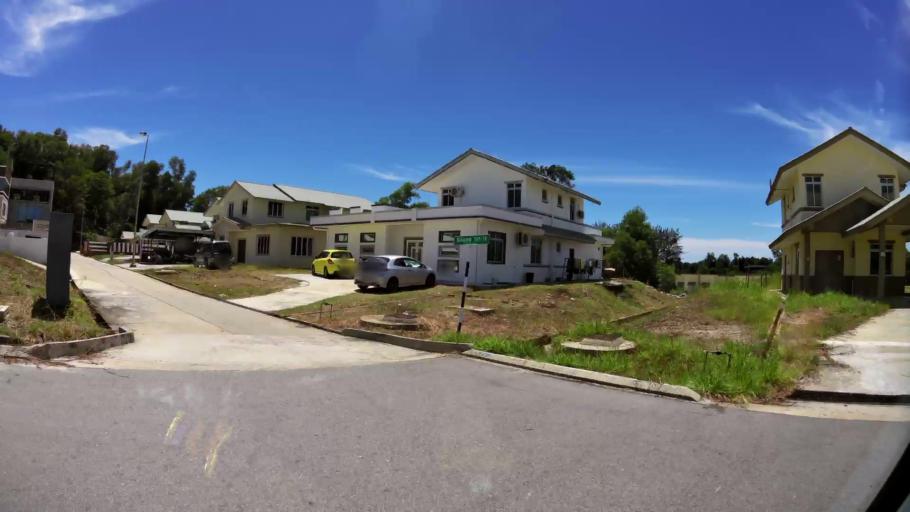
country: BN
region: Brunei and Muara
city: Bandar Seri Begawan
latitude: 5.0320
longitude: 115.0300
